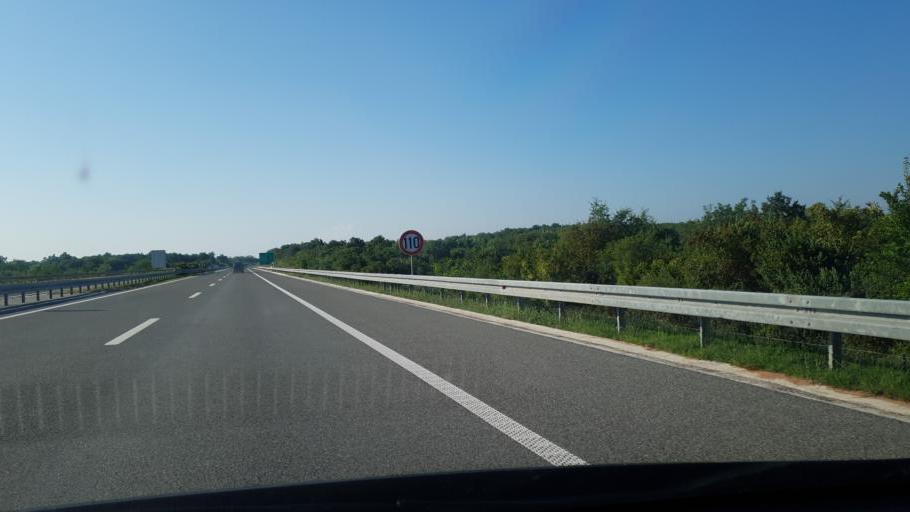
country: HR
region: Istarska
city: Vodnjan
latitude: 44.9911
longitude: 13.8430
